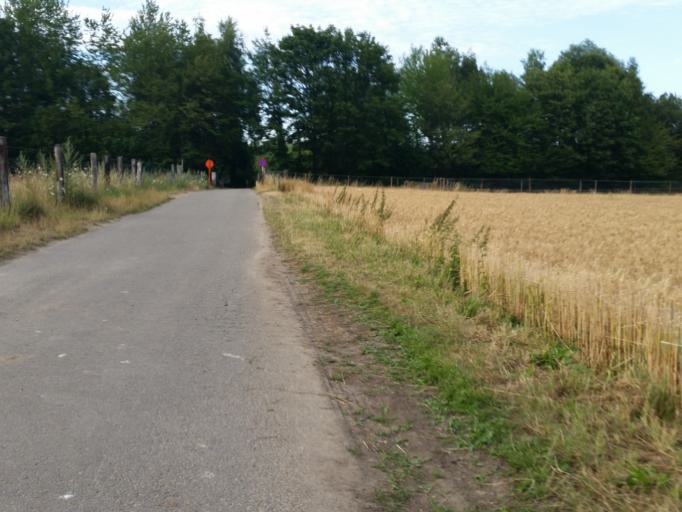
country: BE
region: Flanders
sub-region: Provincie Vlaams-Brabant
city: Zemst
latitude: 50.9756
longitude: 4.4830
